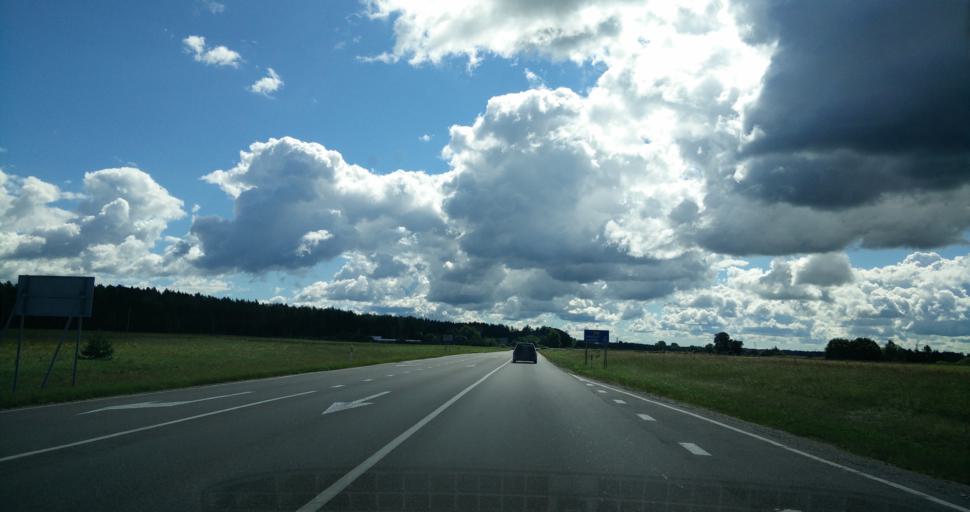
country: LT
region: Klaipedos apskritis
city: Silute
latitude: 55.3315
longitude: 21.5154
